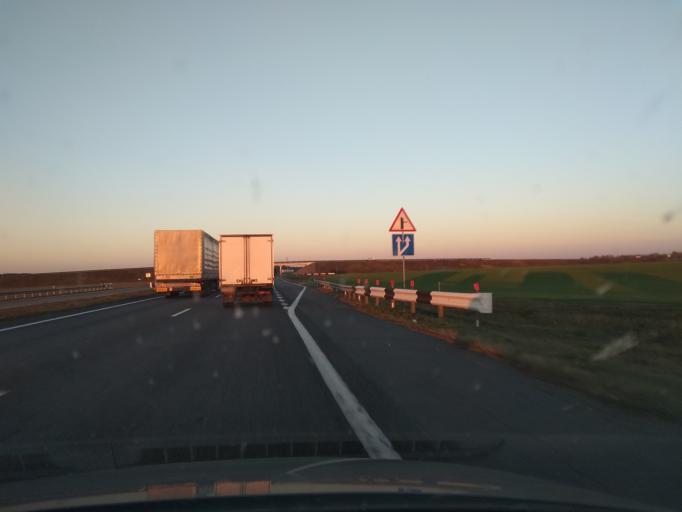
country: BY
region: Minsk
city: Haradzyeya
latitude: 53.4045
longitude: 26.5524
